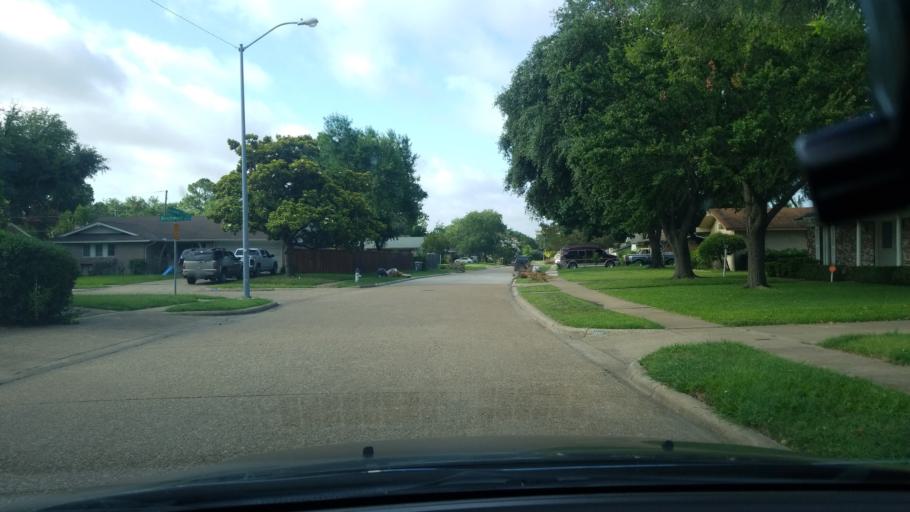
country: US
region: Texas
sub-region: Dallas County
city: Mesquite
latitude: 32.8182
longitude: -96.6861
